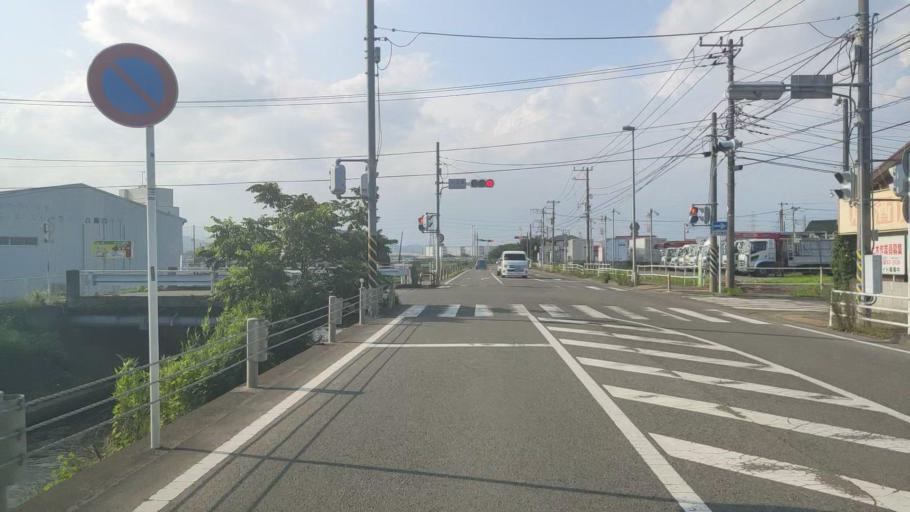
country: JP
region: Kanagawa
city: Isehara
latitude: 35.3902
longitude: 139.3382
